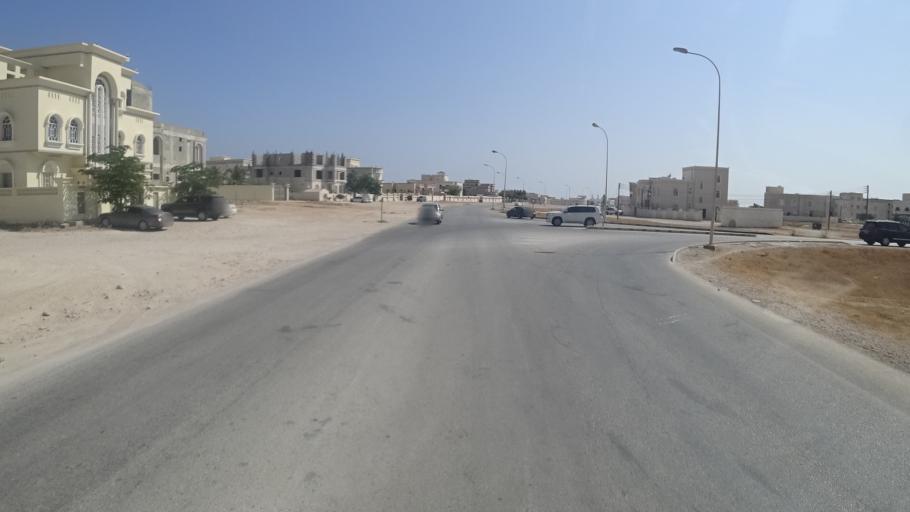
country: OM
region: Zufar
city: Salalah
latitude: 17.0107
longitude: 54.0255
